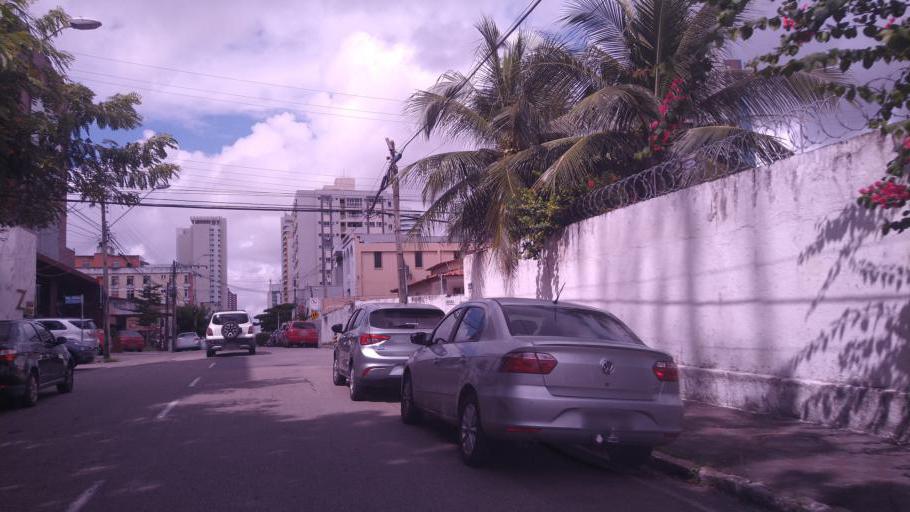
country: BR
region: Ceara
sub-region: Fortaleza
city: Fortaleza
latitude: -3.7335
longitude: -38.4887
